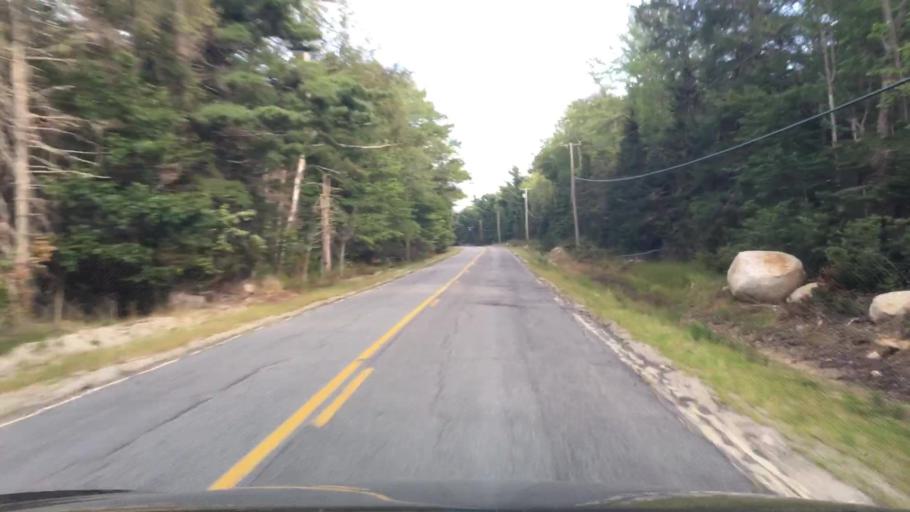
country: US
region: Maine
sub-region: Hancock County
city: Surry
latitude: 44.4989
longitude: -68.5473
